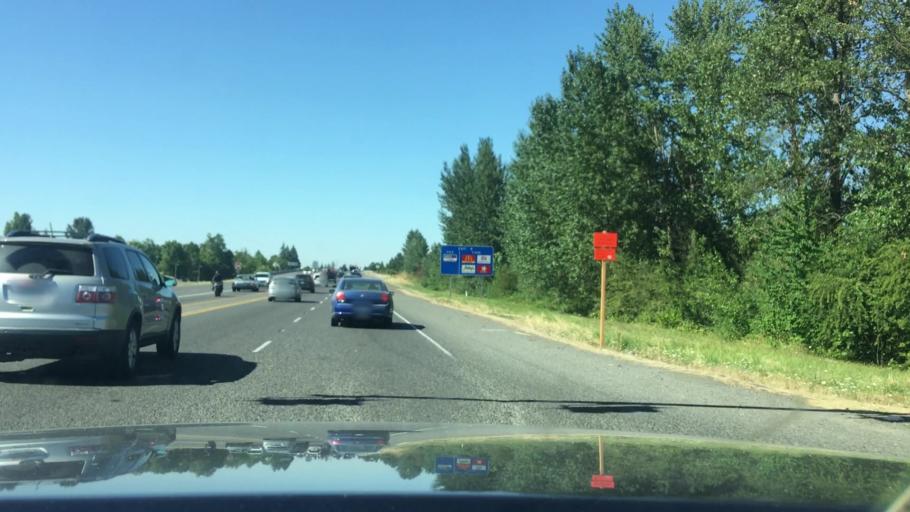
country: US
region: Oregon
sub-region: Lane County
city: Eugene
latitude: 44.0648
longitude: -123.1736
